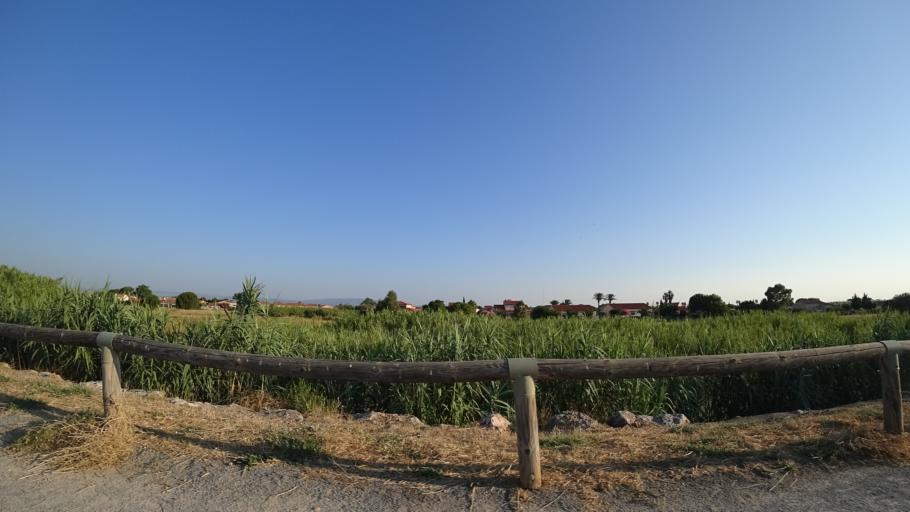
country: FR
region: Languedoc-Roussillon
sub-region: Departement des Pyrenees-Orientales
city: Saint-Laurent-de-la-Salanque
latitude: 42.7701
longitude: 3.0112
